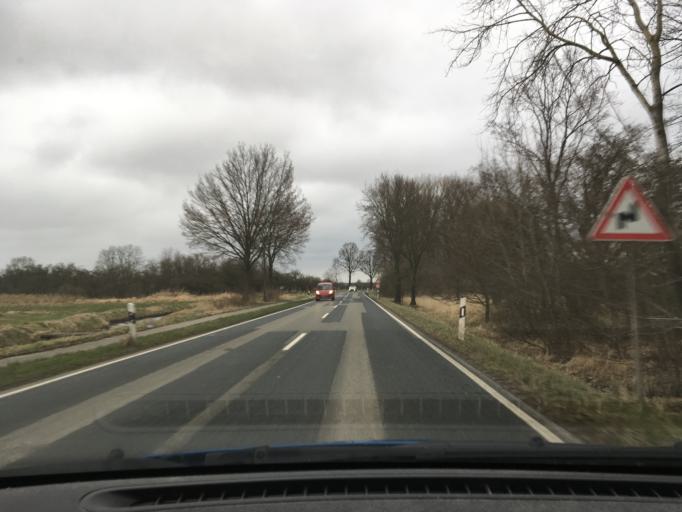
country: DE
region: Lower Saxony
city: Drage
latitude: 53.3997
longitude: 10.2583
